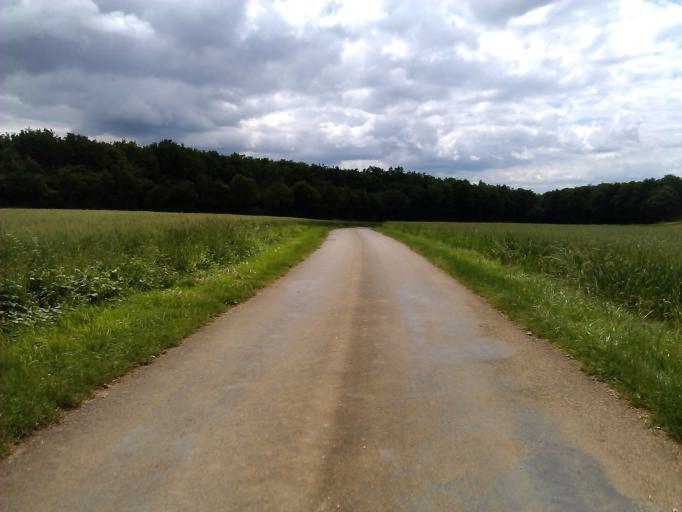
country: FR
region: Poitou-Charentes
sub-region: Departement de la Charente
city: Nanteuil-en-Vallee
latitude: 45.9590
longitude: 0.2742
